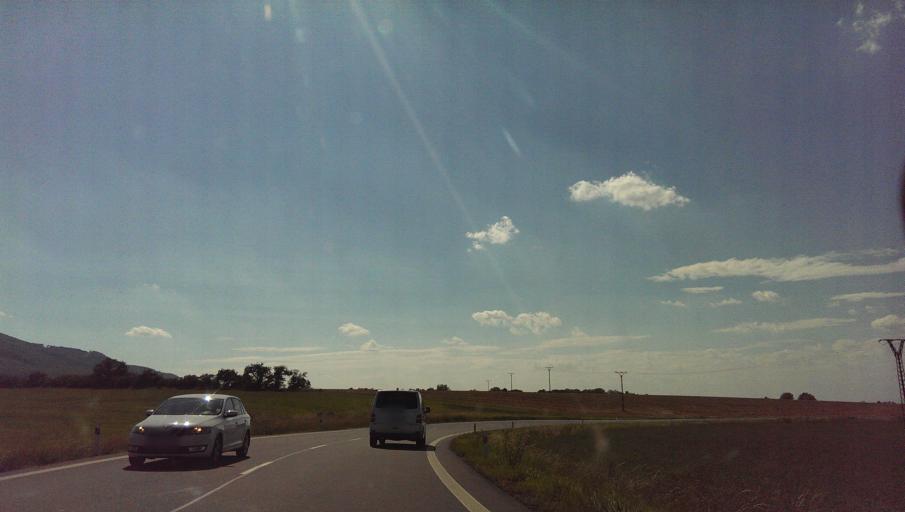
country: CZ
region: Zlin
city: Kelc
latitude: 49.4337
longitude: 17.7945
